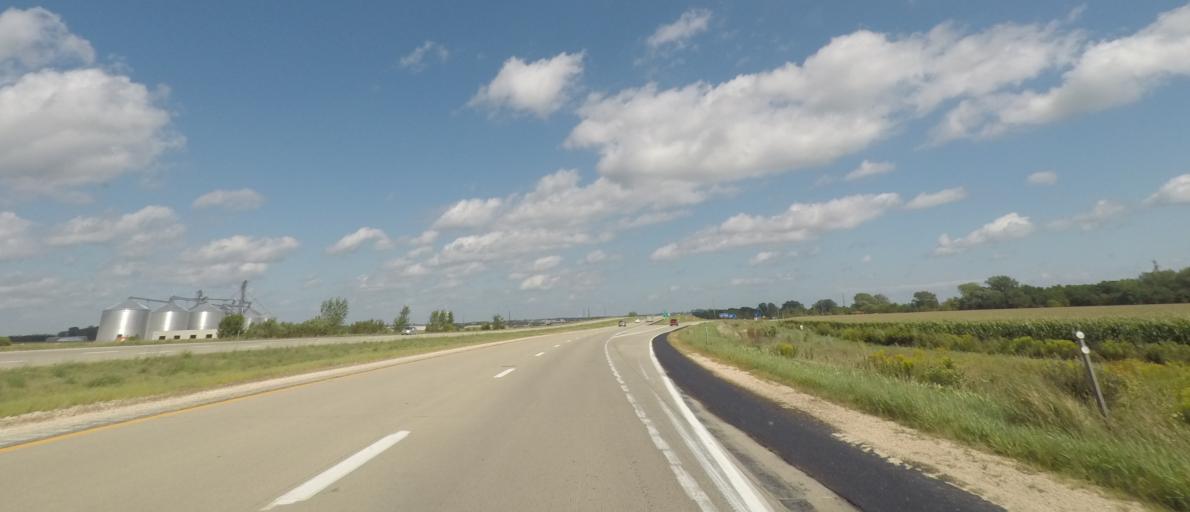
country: US
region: Iowa
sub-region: Jones County
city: Monticello
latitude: 42.2064
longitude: -91.1973
